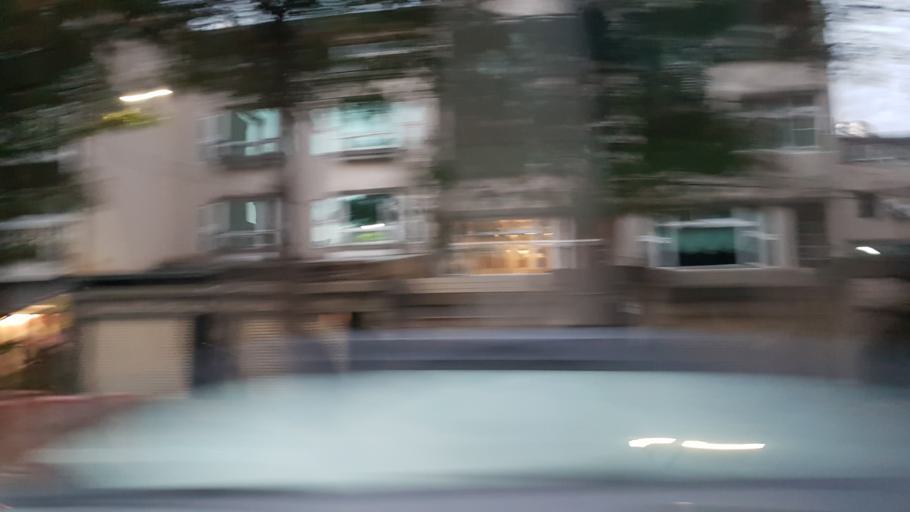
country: TW
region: Taiwan
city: Xinying
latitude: 23.3083
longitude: 120.2972
